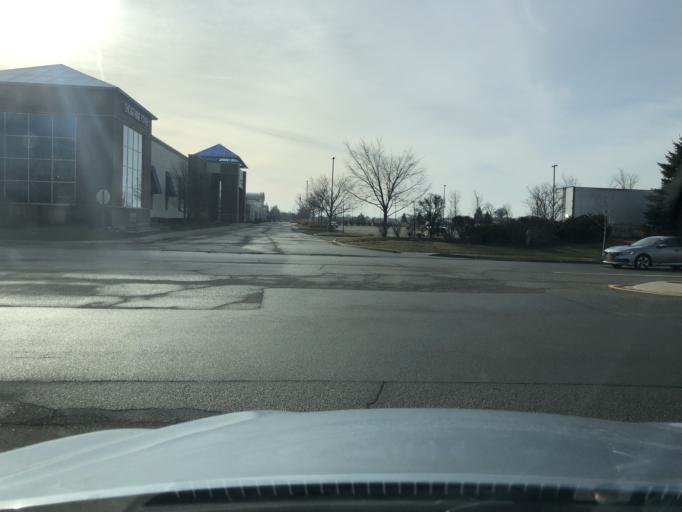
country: US
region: Illinois
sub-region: McHenry County
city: Lake in the Hills
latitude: 42.1357
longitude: -88.3343
